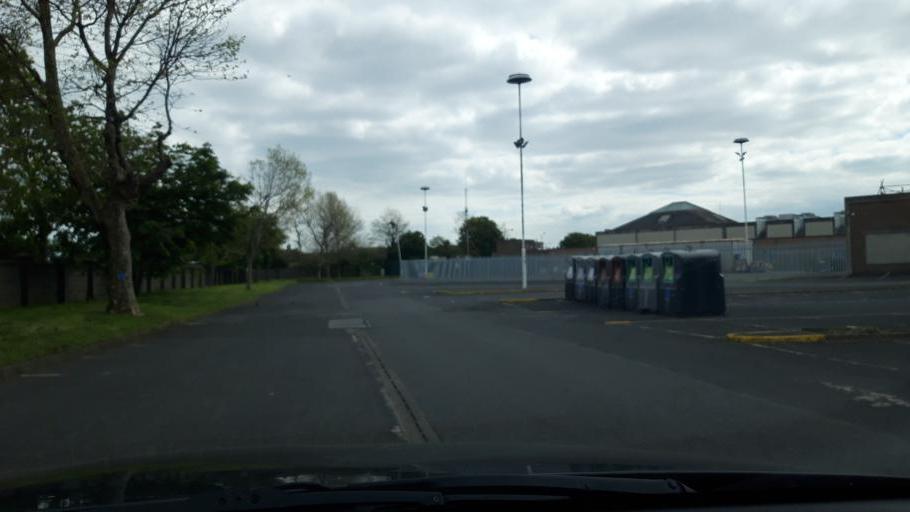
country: IE
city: Greenhills
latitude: 53.3312
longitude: -6.3019
